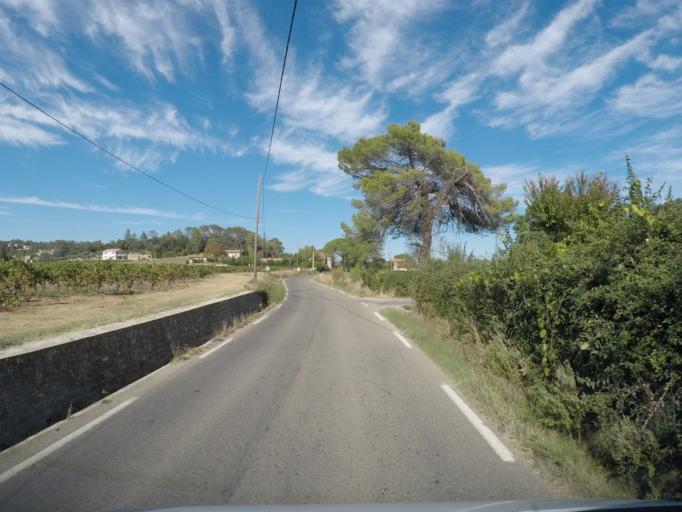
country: FR
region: Languedoc-Roussillon
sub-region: Departement du Gard
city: Boisset-et-Gaujac
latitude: 44.0188
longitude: 3.9944
